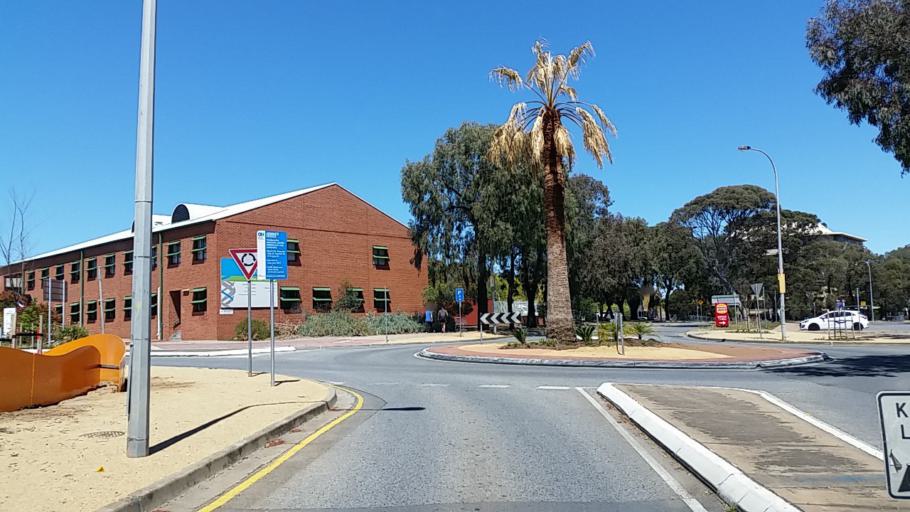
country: AU
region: South Australia
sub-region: Onkaparinga
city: Noarlunga Downs
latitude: -35.1385
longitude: 138.4970
